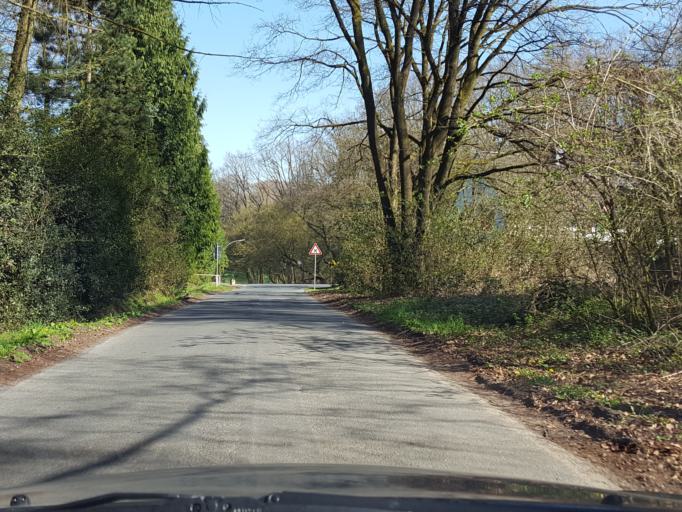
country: DE
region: North Rhine-Westphalia
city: Oer-Erkenschwick
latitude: 51.6567
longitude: 7.2341
